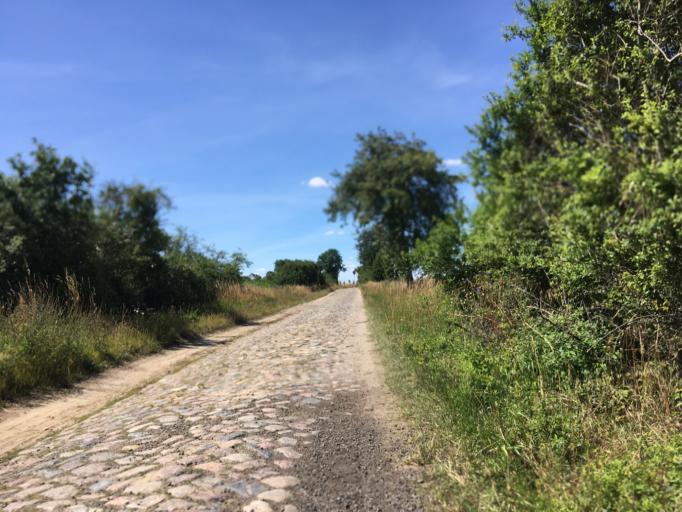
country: DE
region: Brandenburg
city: Brussow
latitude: 53.3210
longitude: 14.1070
